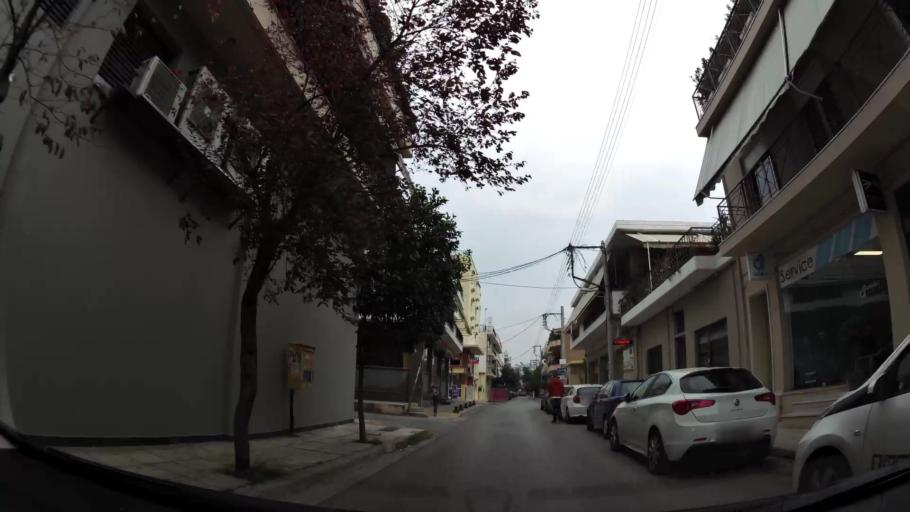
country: GR
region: Attica
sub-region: Nomarchia Athinas
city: Chaidari
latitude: 38.0051
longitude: 23.6753
